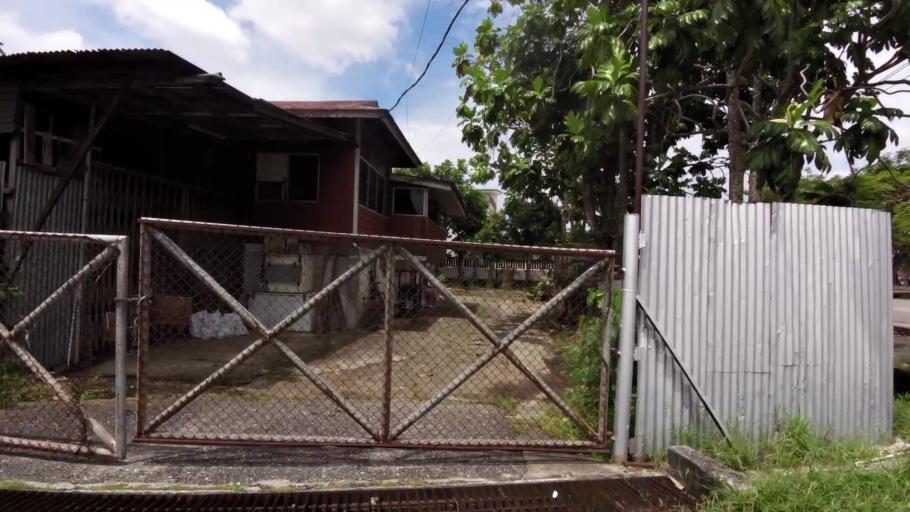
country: BN
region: Brunei and Muara
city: Bandar Seri Begawan
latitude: 4.9456
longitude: 114.9454
